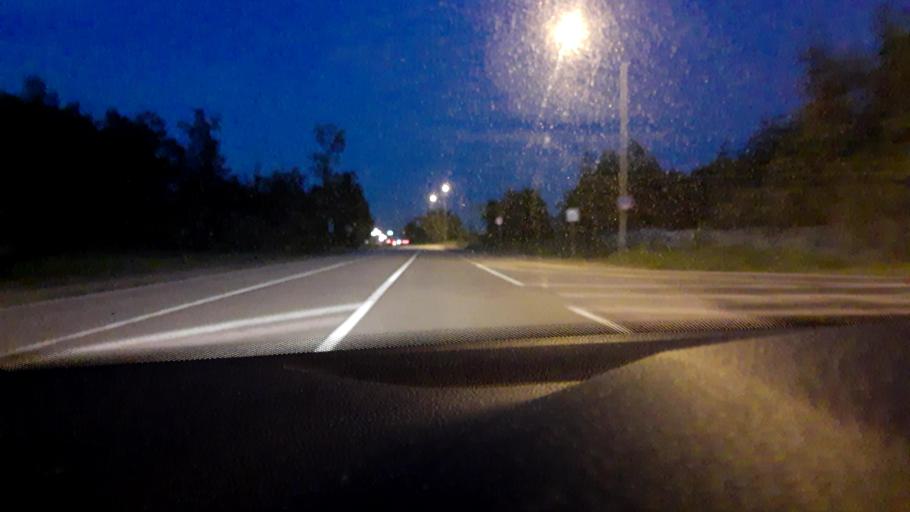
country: RU
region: Moskovskaya
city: Opalikha
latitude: 55.7863
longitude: 37.2275
